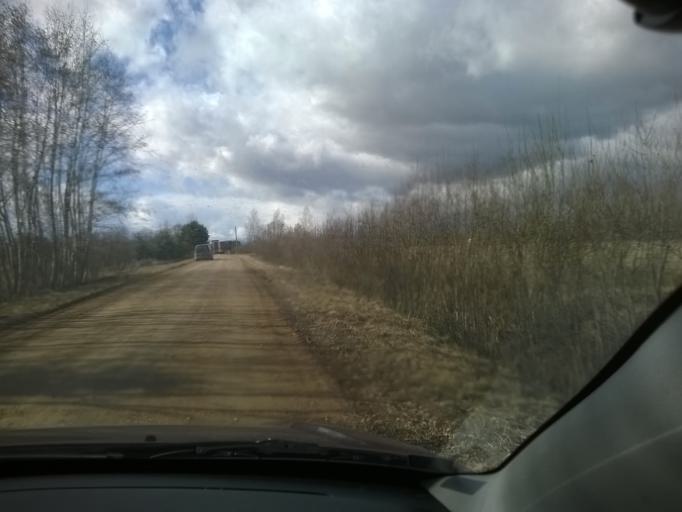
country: EE
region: Tartu
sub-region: Alatskivi vald
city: Kallaste
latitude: 58.3817
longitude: 27.0788
